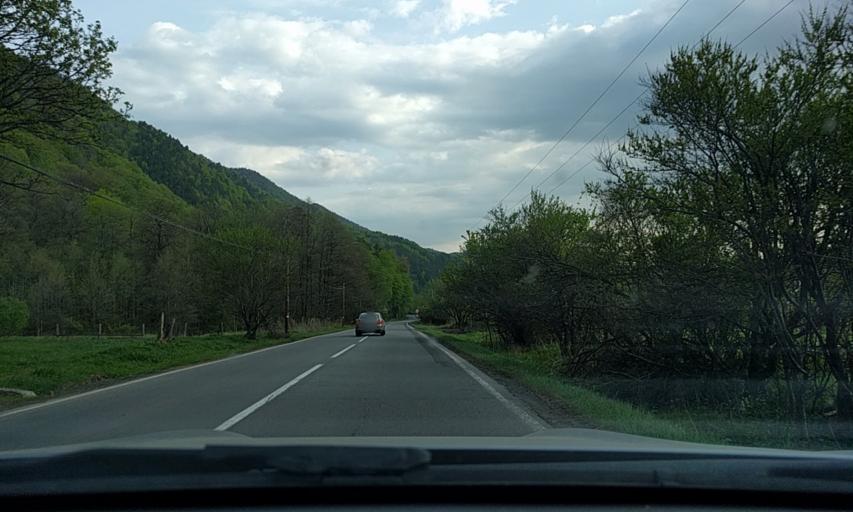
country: RO
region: Bacau
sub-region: Oras Slanic-Moldova
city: Slanic-Moldova
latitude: 46.1536
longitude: 26.4597
